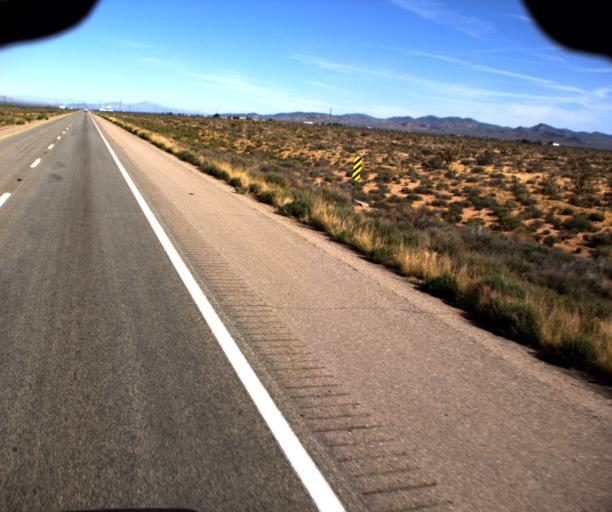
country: US
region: Arizona
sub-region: Mohave County
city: Dolan Springs
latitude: 35.5230
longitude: -114.3476
